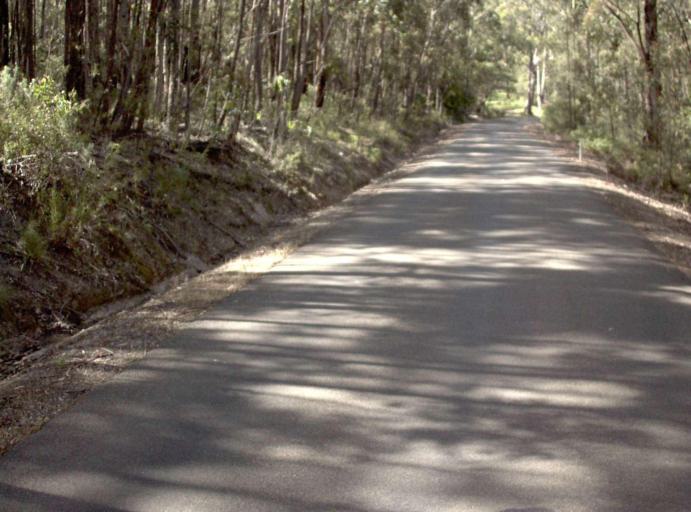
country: AU
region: Victoria
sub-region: East Gippsland
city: Lakes Entrance
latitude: -37.4424
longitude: 148.1315
